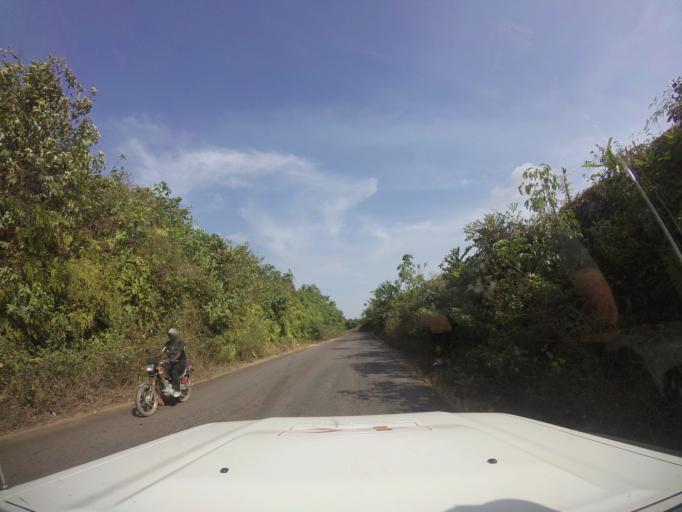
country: LR
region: Bomi
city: Tubmanburg
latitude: 6.7045
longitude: -10.9226
